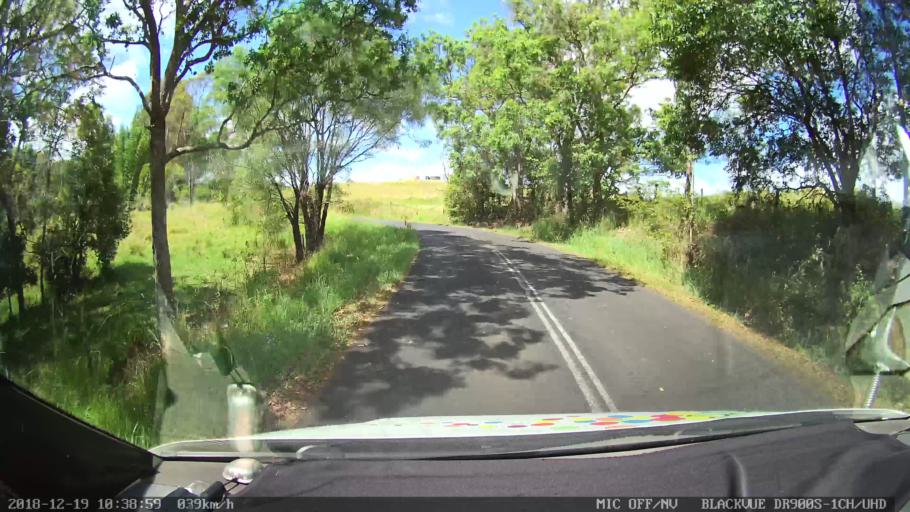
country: AU
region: New South Wales
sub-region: Lismore Municipality
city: Nimbin
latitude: -28.5779
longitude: 153.1546
